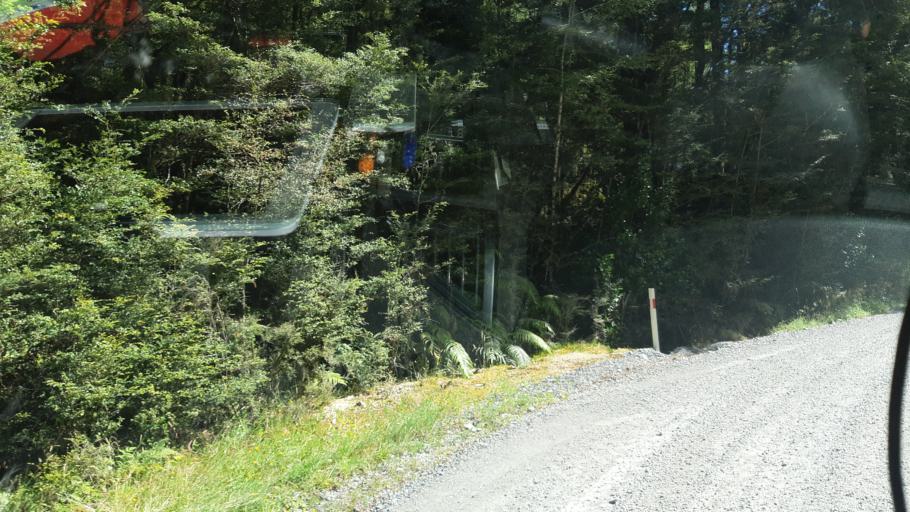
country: NZ
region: West Coast
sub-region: Buller District
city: Westport
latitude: -42.2912
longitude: 172.1856
